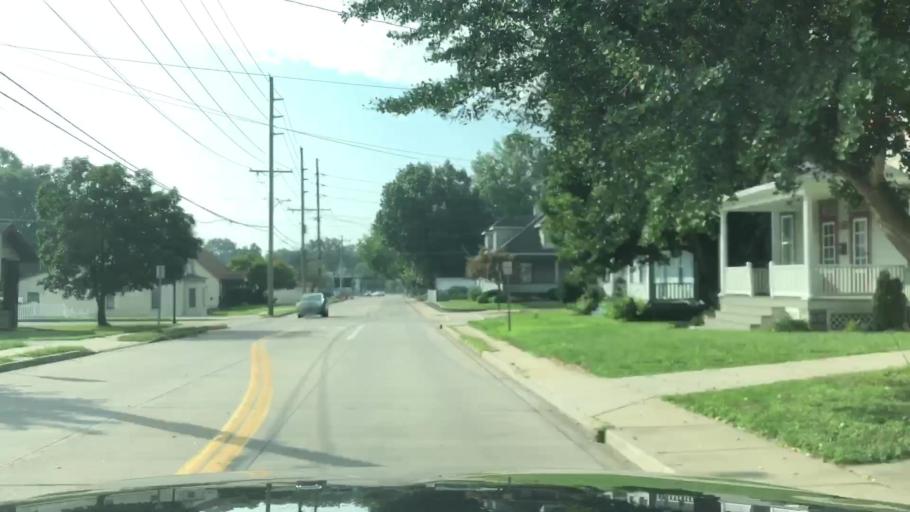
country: US
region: Missouri
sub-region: Saint Charles County
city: Saint Charles
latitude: 38.7892
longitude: -90.4948
